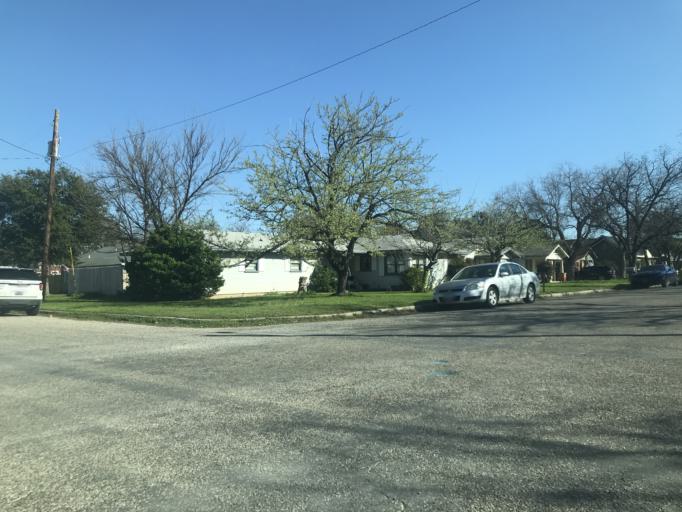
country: US
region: Texas
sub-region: Tom Green County
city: San Angelo
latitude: 31.4462
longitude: -100.4459
